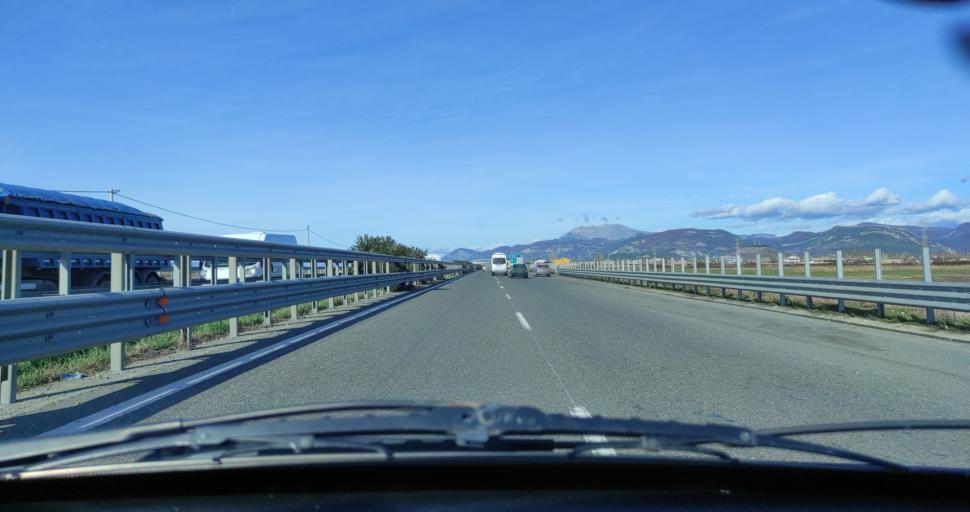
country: AL
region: Lezhe
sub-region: Rrethi i Kurbinit
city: Lac
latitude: 41.6413
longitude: 19.6729
